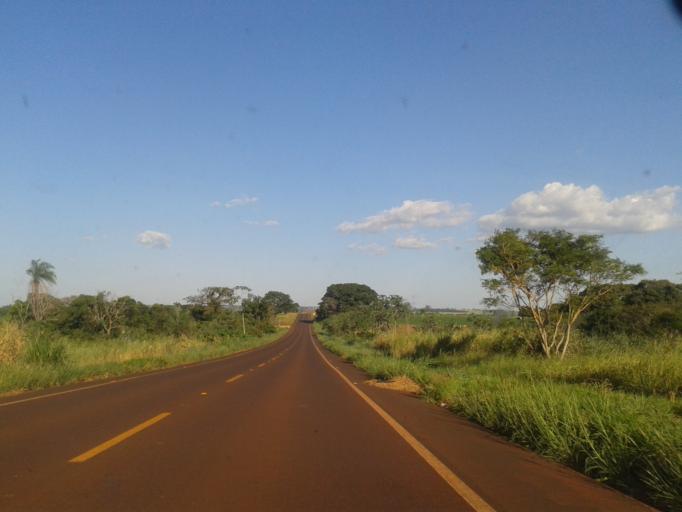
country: BR
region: Minas Gerais
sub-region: Santa Vitoria
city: Santa Vitoria
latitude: -18.7002
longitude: -49.8732
